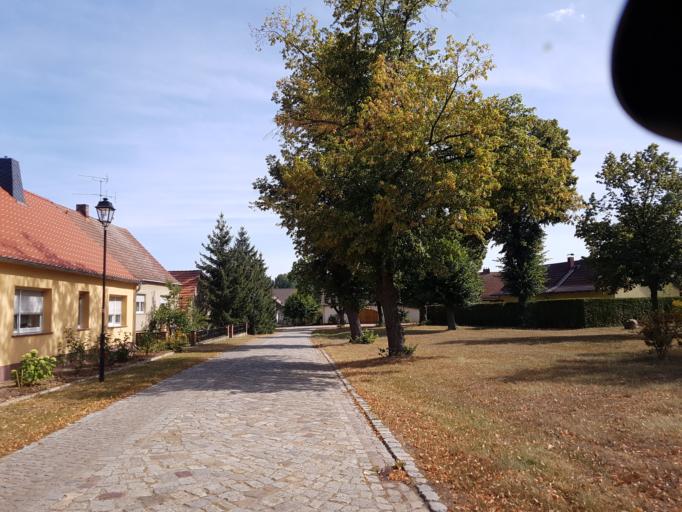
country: DE
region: Brandenburg
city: Drahnsdorf
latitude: 51.8609
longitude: 13.6263
